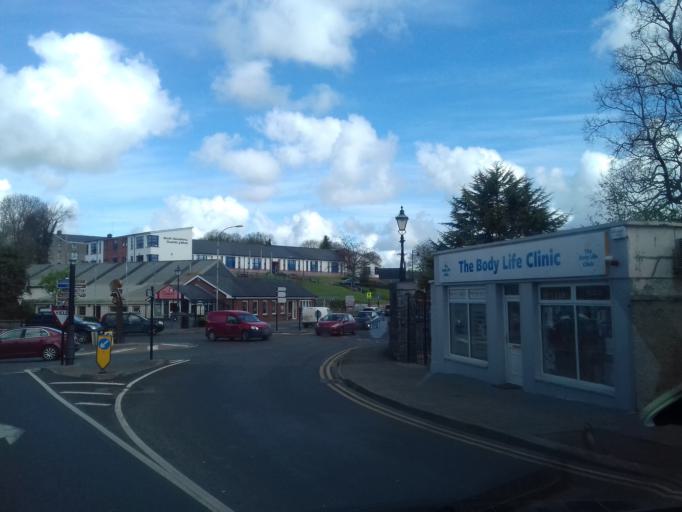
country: IE
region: Ulster
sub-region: An Cabhan
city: Cavan
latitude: 53.9896
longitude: -7.3633
